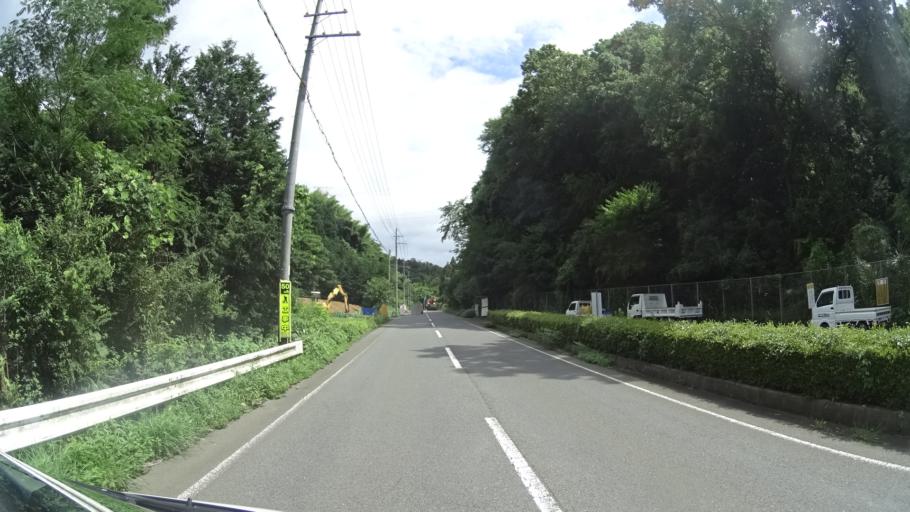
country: JP
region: Kyoto
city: Ayabe
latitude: 35.3513
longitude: 135.2733
